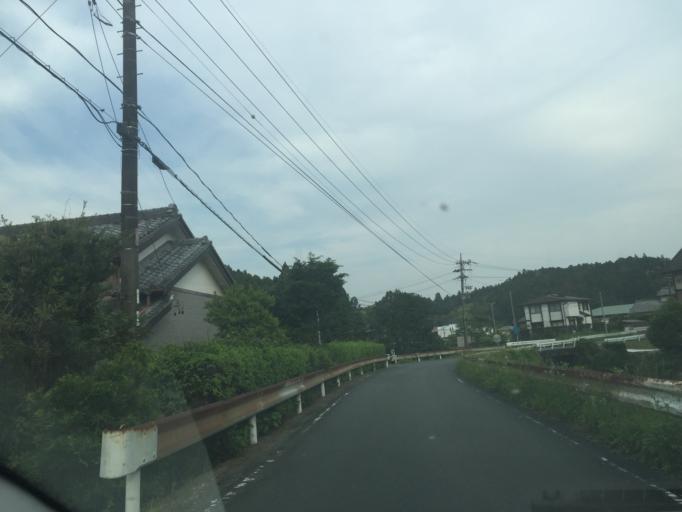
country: JP
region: Shizuoka
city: Kakegawa
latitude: 34.8203
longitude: 138.0174
